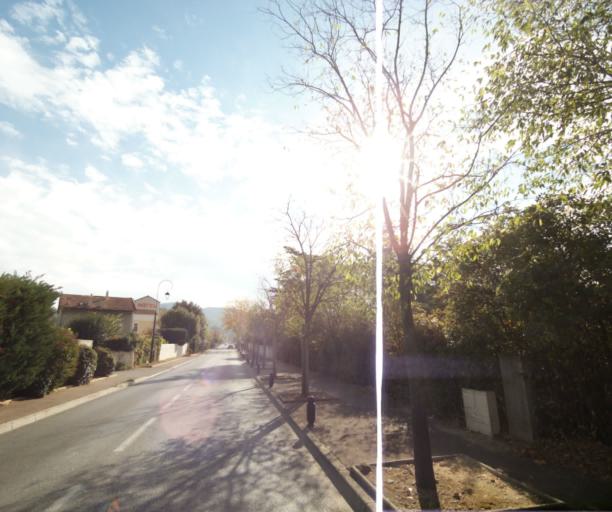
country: FR
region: Provence-Alpes-Cote d'Azur
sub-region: Departement des Bouches-du-Rhone
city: Gemenos
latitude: 43.2995
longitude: 5.6206
